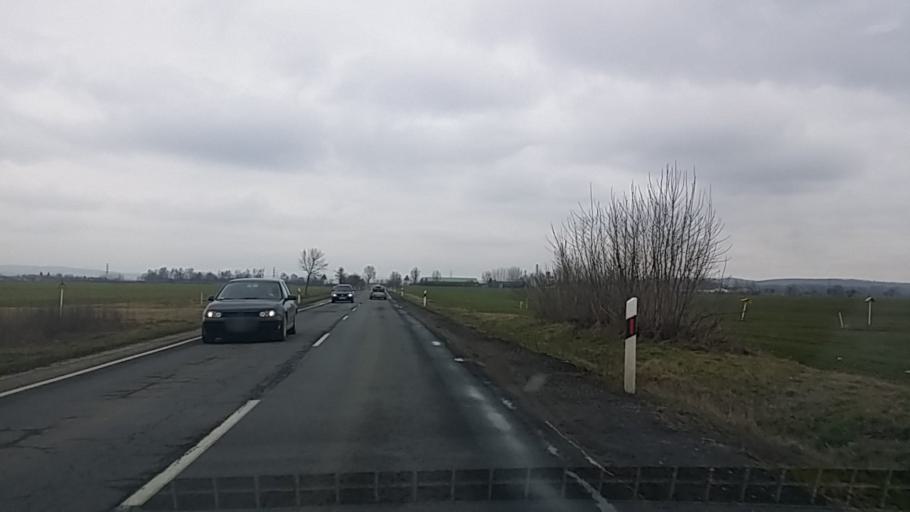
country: HU
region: Borsod-Abauj-Zemplen
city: Sajoszentpeter
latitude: 48.2259
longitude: 20.7277
